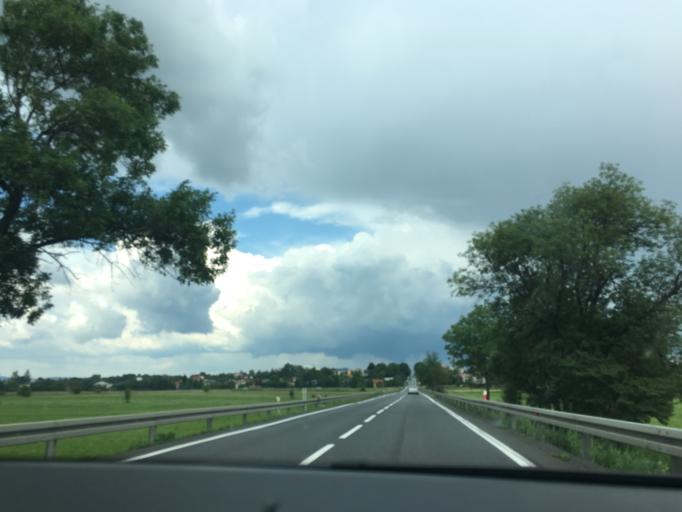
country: PL
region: Subcarpathian Voivodeship
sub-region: Powiat krosnienski
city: Miejsce Piastowe
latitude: 49.6417
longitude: 21.8014
